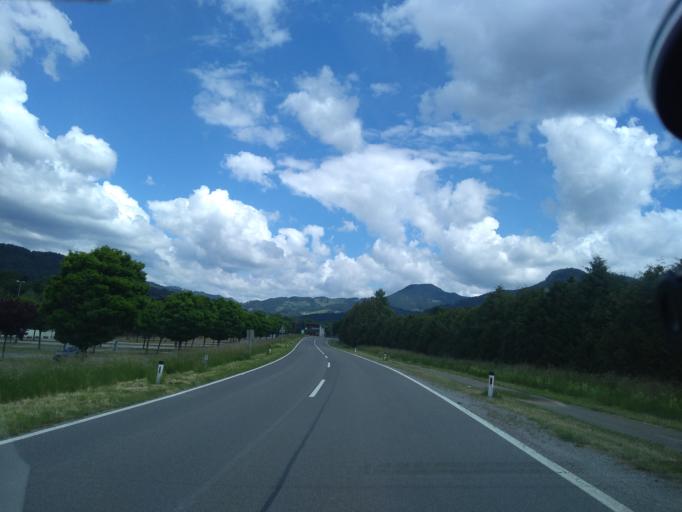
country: AT
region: Styria
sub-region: Politischer Bezirk Graz-Umgebung
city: Frohnleiten
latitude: 47.2559
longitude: 15.3208
